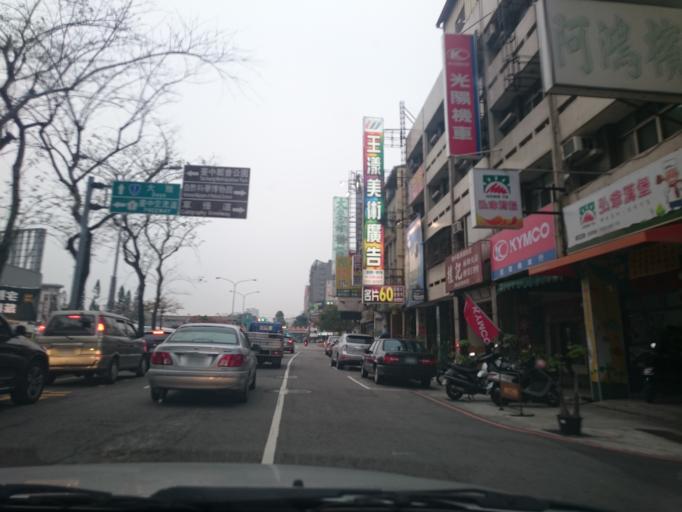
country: TW
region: Taiwan
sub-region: Taichung City
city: Taichung
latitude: 24.1558
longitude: 120.6597
